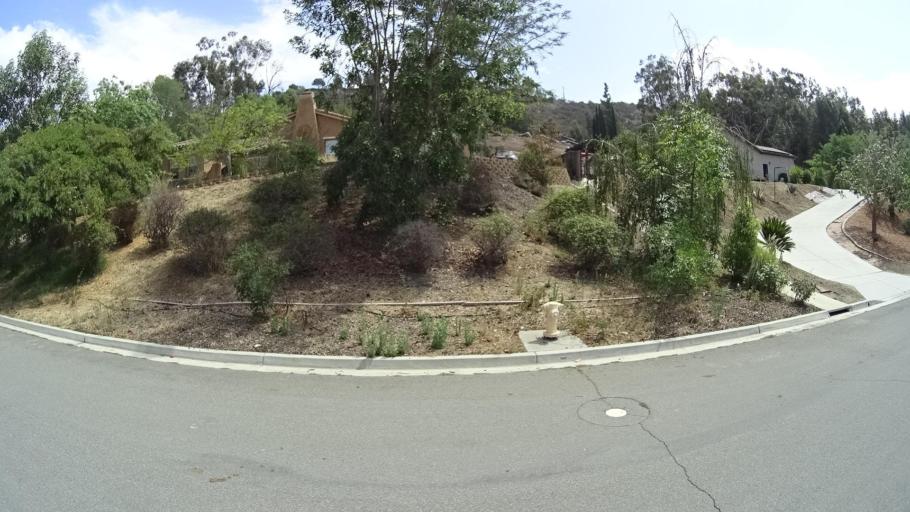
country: US
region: California
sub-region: San Diego County
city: Hidden Meadows
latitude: 33.1849
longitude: -117.0897
